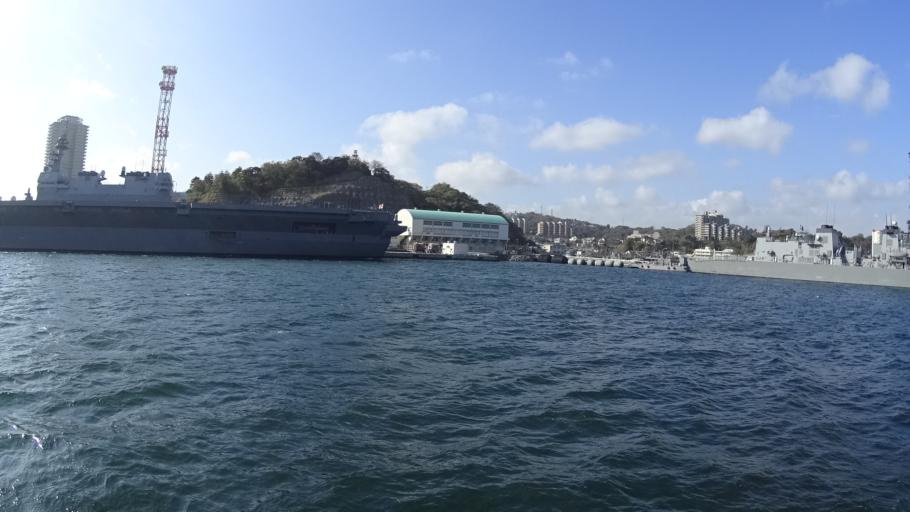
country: JP
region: Kanagawa
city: Yokosuka
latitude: 35.2889
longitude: 139.6547
